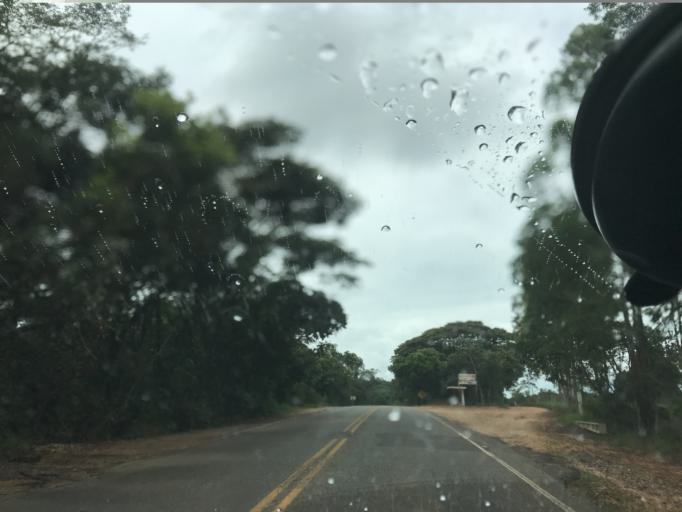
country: BR
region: Minas Gerais
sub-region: Conceicao Do Rio Verde
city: Conceicao do Rio Verde
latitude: -21.6842
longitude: -45.0163
